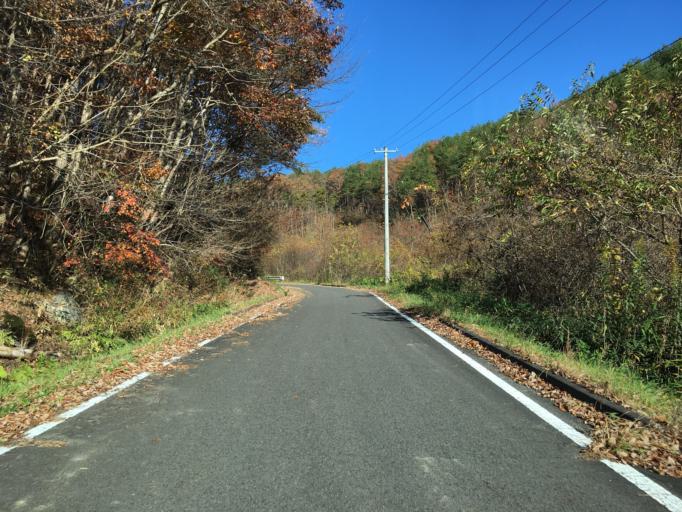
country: JP
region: Fukushima
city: Ishikawa
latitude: 37.2364
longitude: 140.5229
